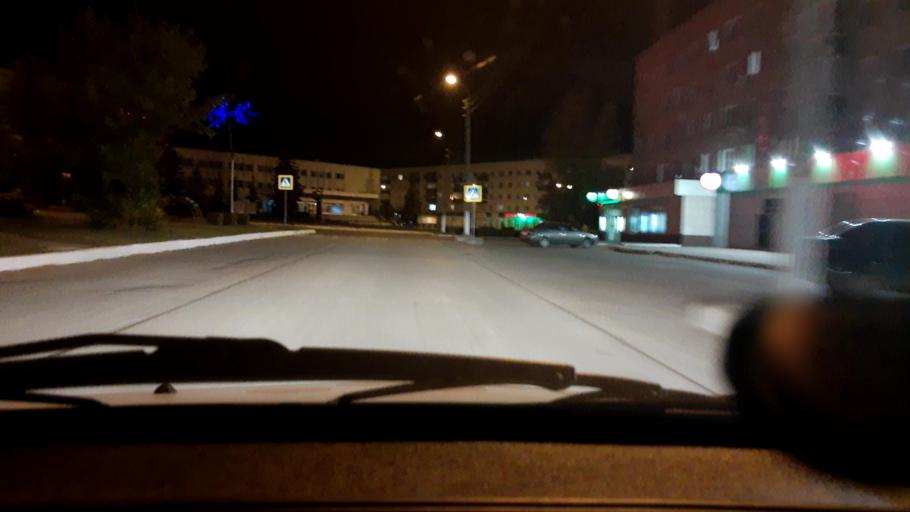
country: RU
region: Bashkortostan
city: Belebey
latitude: 54.1020
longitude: 54.1018
